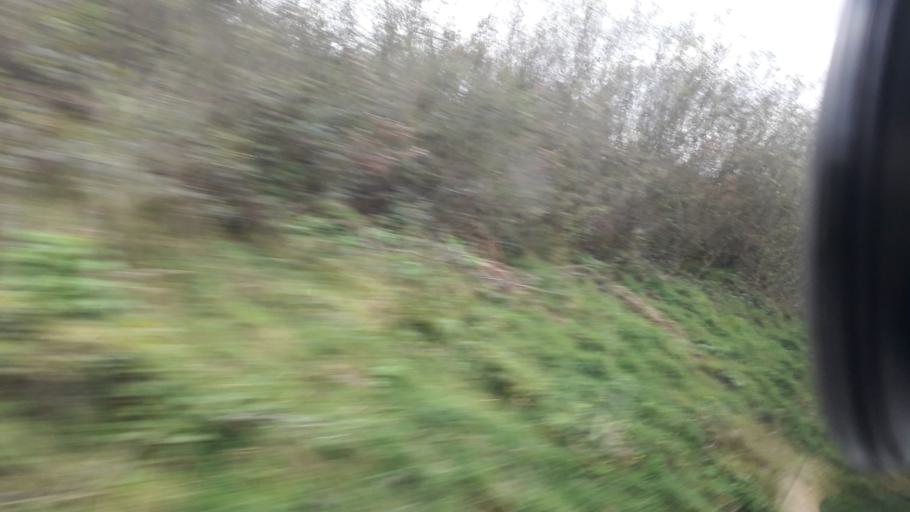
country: IE
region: Leinster
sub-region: An Iarmhi
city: An Muileann gCearr
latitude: 53.6079
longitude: -7.4033
